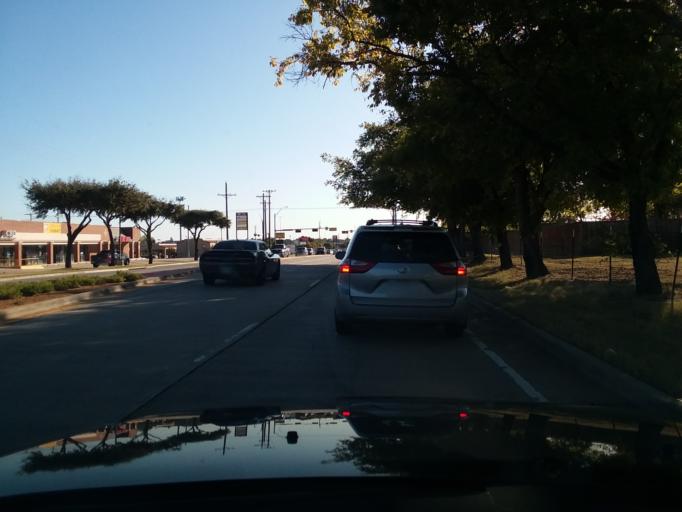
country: US
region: Texas
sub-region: Denton County
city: Highland Village
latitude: 33.0713
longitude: -97.0287
